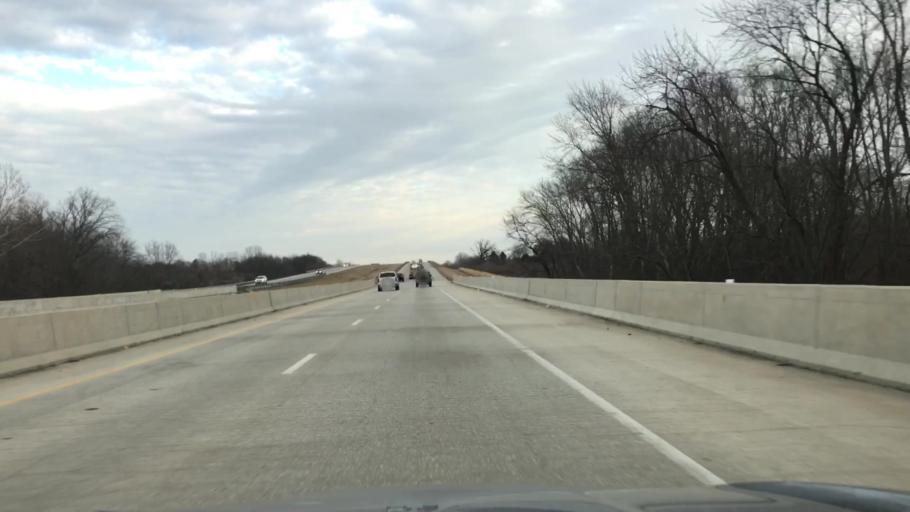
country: US
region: Illinois
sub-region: Logan County
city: Lincoln
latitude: 40.1814
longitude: -89.3703
